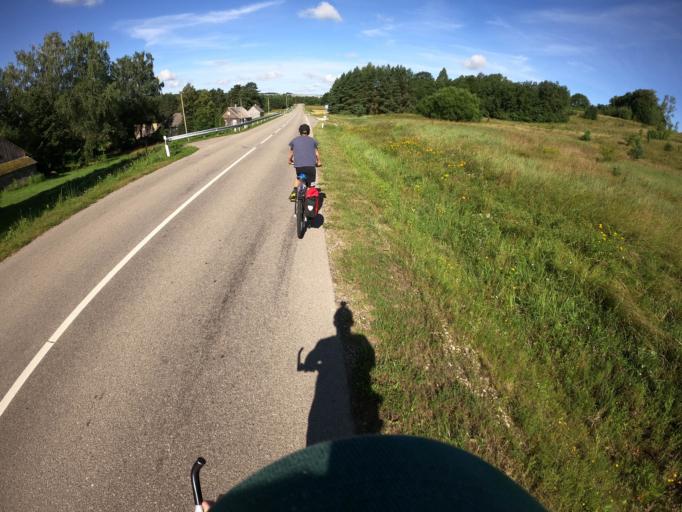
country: LT
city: Raseiniai
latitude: 55.5016
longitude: 23.1067
